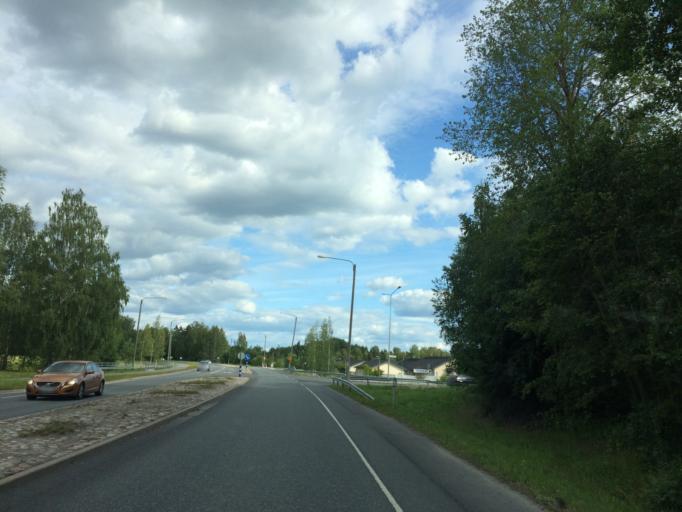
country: FI
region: Haeme
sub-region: Haemeenlinna
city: Janakkala
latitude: 60.9629
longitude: 24.5538
